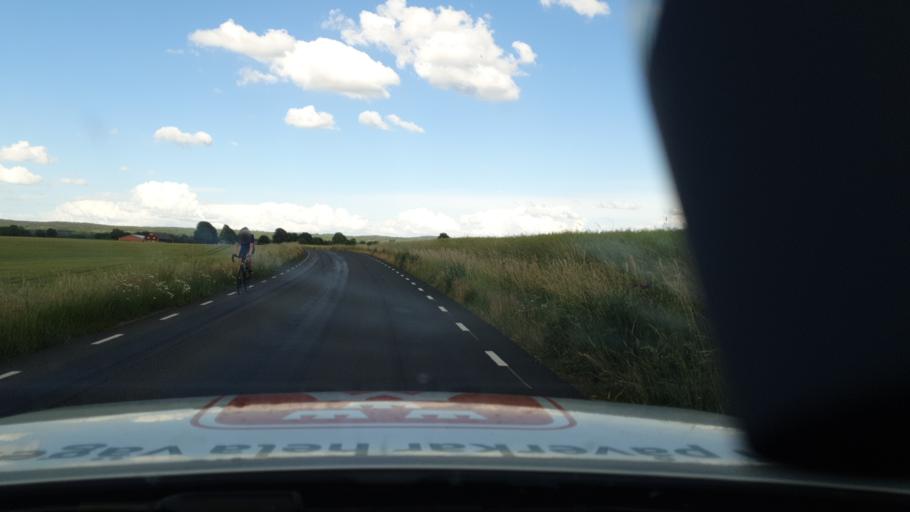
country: SE
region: Vaestra Goetaland
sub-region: Skara Kommun
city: Axvall
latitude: 58.3852
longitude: 13.6236
